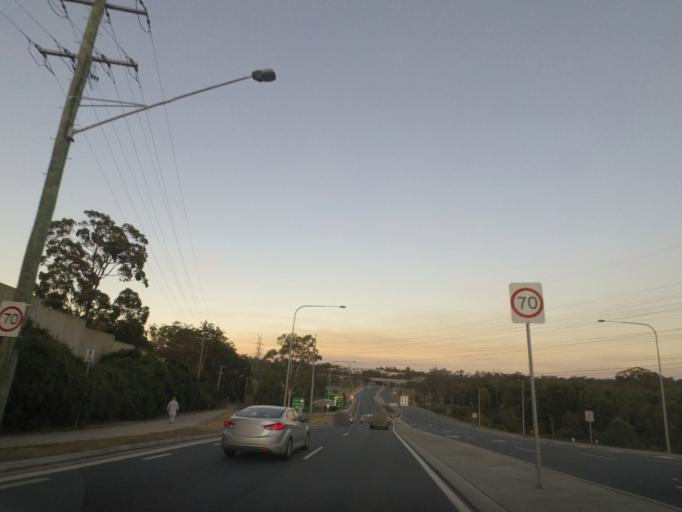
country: AU
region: Queensland
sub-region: Brisbane
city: Mackenzie
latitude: -27.5464
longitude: 153.1118
